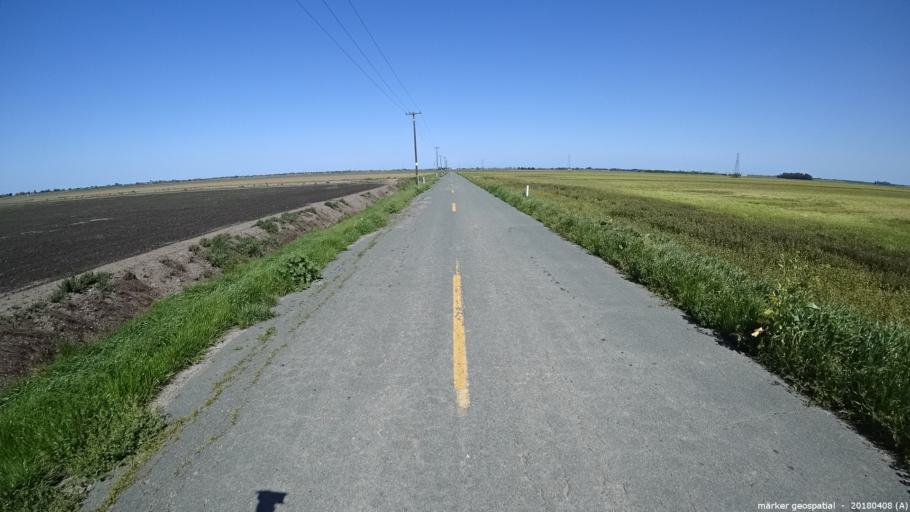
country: US
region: California
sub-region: Sacramento County
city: Walnut Grove
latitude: 38.3046
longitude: -121.5574
